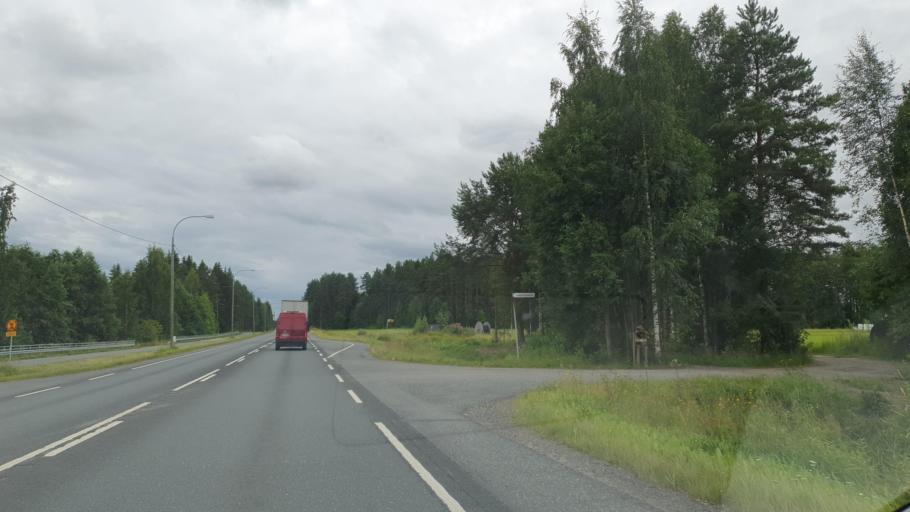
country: FI
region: Northern Savo
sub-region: Ylae-Savo
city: Lapinlahti
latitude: 63.4701
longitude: 27.3039
